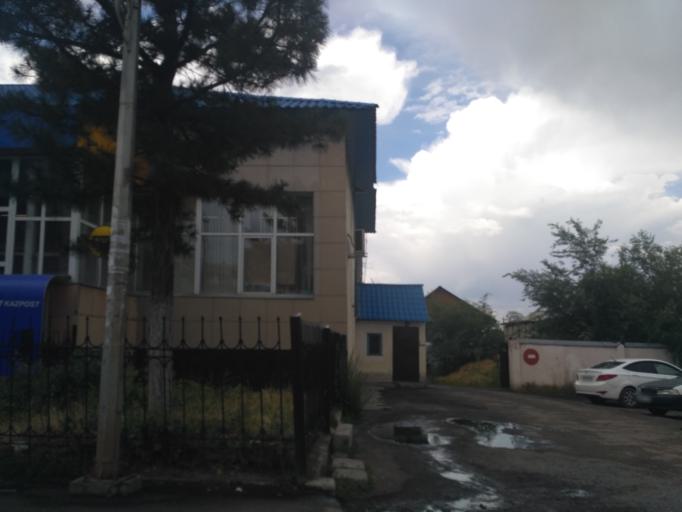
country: KZ
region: Almaty Oblysy
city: Burunday
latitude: 43.2019
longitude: 76.6255
